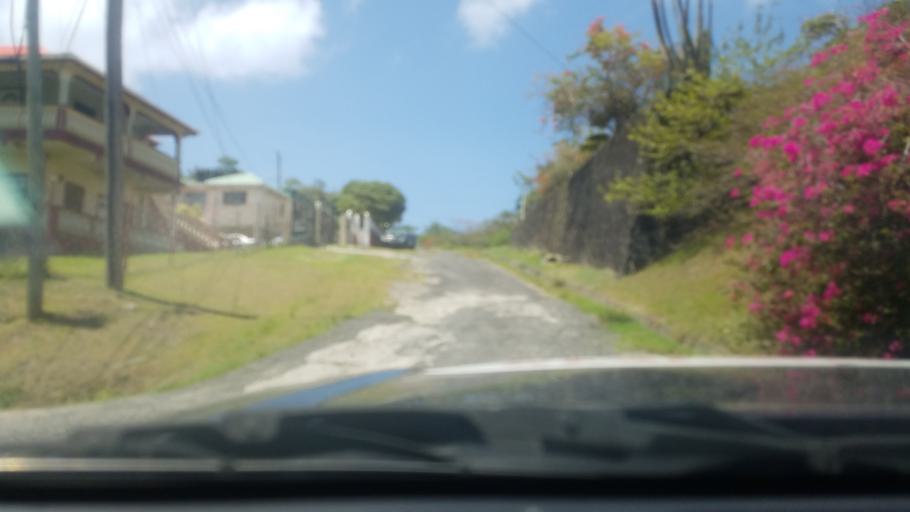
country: LC
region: Vieux-Fort
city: Vieux Fort
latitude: 13.7181
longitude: -60.9514
